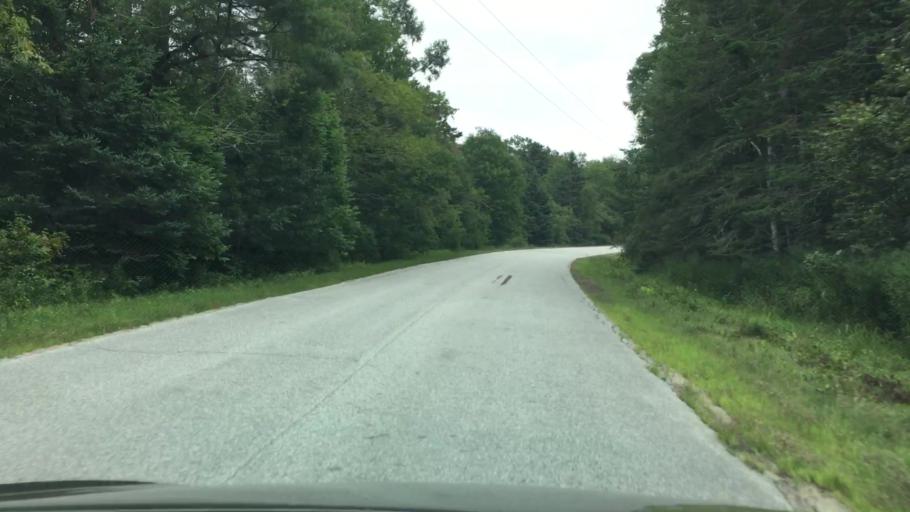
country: US
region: Maine
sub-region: Waldo County
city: Stockton Springs
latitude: 44.5255
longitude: -68.8213
